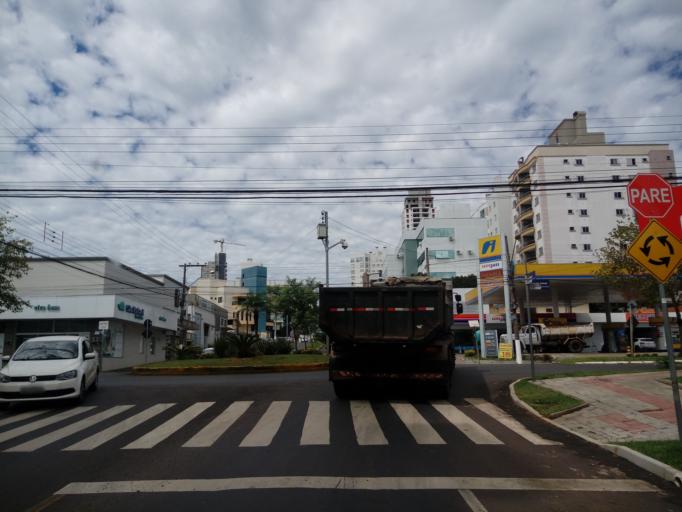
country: BR
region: Santa Catarina
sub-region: Chapeco
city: Chapeco
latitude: -27.0988
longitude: -52.6093
